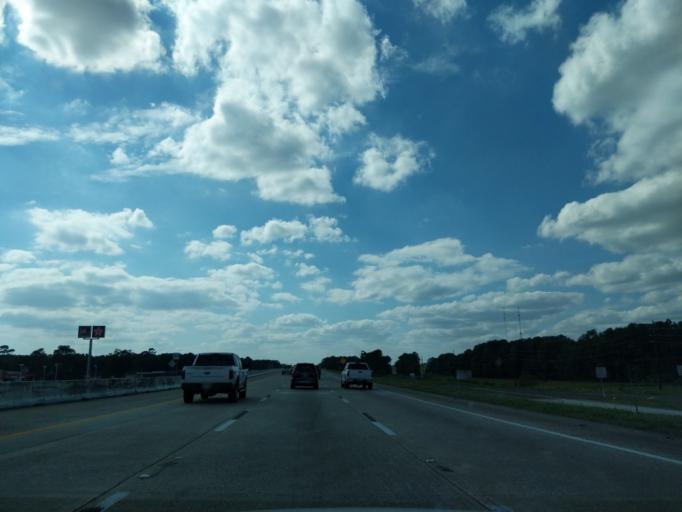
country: US
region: Texas
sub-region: Chambers County
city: Anahuac
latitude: 29.8406
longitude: -94.6906
